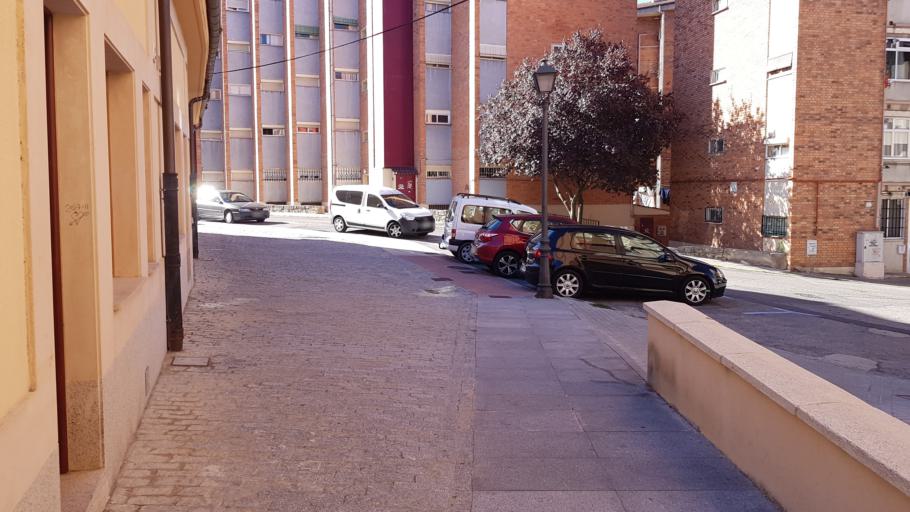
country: ES
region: Castille and Leon
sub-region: Provincia de Segovia
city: Segovia
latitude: 40.9449
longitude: -4.1117
